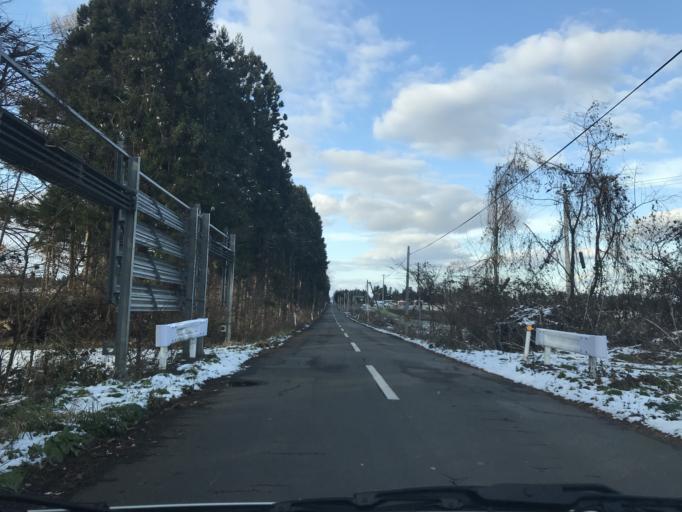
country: JP
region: Iwate
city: Kitakami
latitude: 39.2367
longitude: 141.0329
